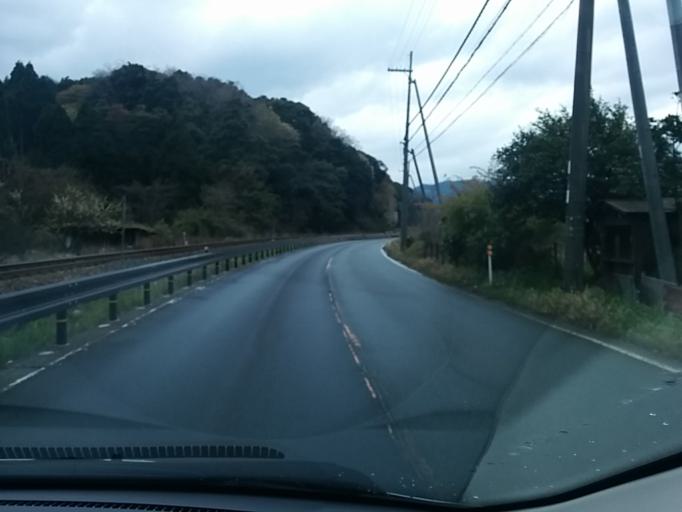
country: JP
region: Kyoto
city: Miyazu
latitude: 35.5607
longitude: 135.1760
